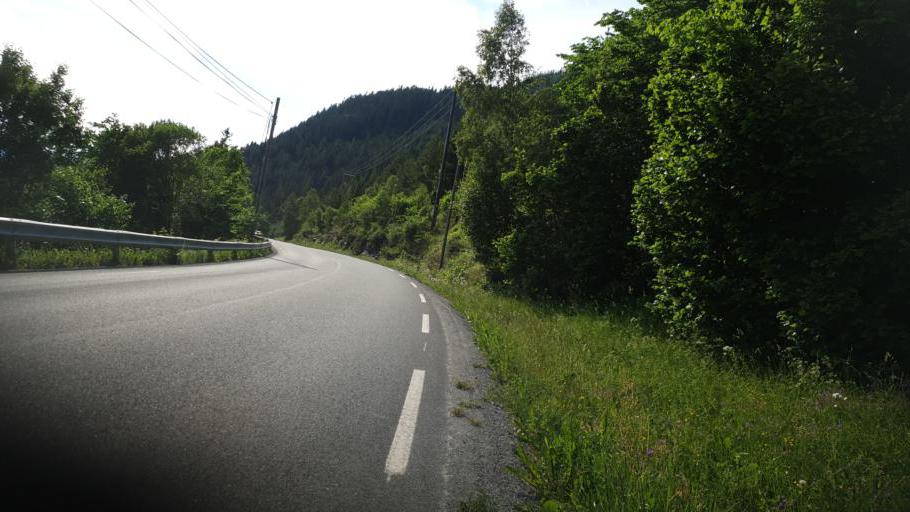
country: NO
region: Sor-Trondelag
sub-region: Trondheim
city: Trondheim
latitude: 63.5576
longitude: 10.2789
